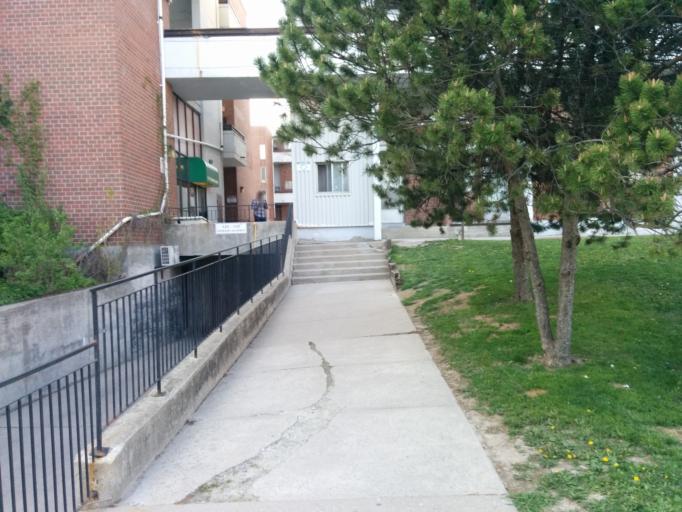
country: CA
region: Ontario
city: Toronto
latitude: 43.7118
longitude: -79.3283
